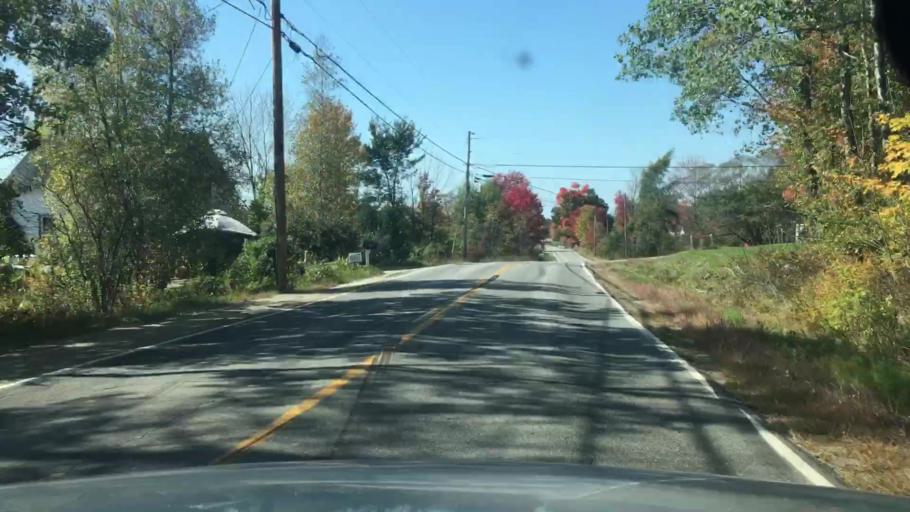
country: US
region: Maine
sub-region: Androscoggin County
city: Lisbon Falls
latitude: 44.0402
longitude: -69.9993
